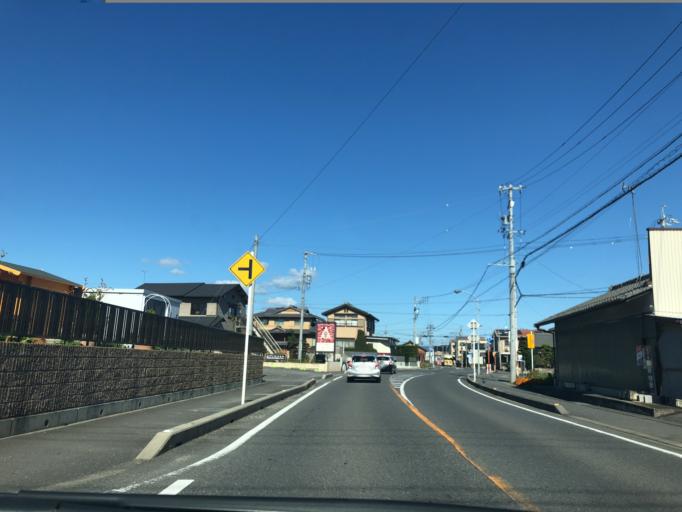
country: JP
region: Gifu
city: Ogaki
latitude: 35.3850
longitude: 136.6669
